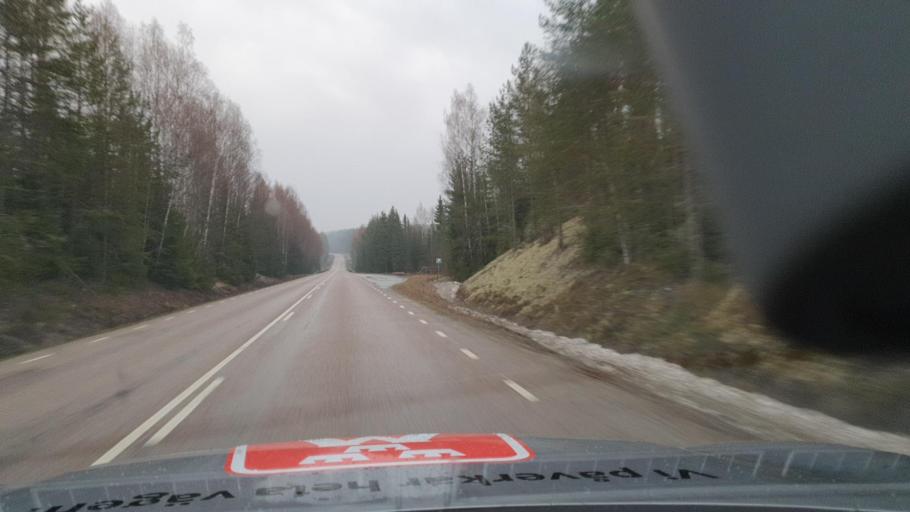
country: SE
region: Vaesternorrland
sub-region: OErnskoeldsviks Kommun
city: Bjasta
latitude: 63.2356
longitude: 18.4434
